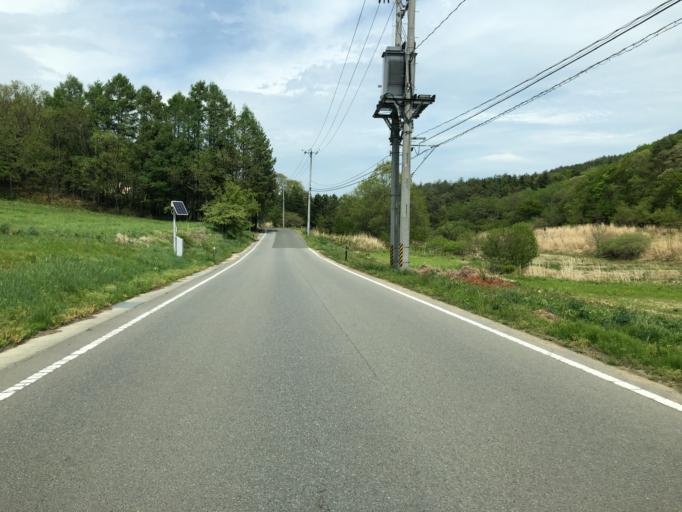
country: JP
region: Fukushima
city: Yanagawamachi-saiwaicho
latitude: 37.7290
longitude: 140.6851
